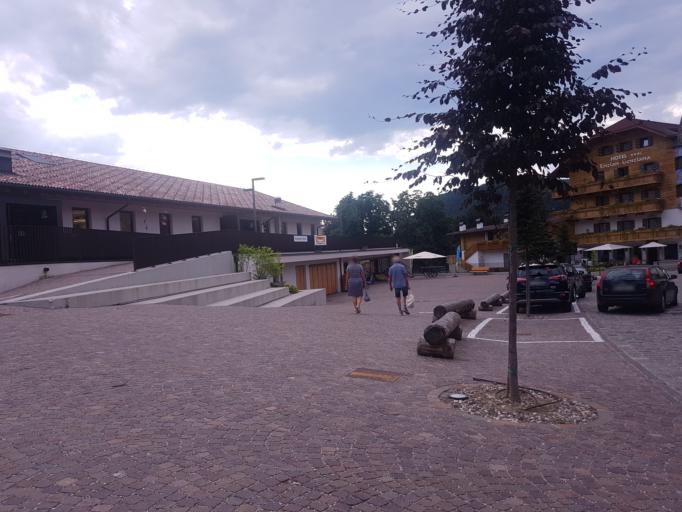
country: IT
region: Trentino-Alto Adige
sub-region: Bolzano
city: Siusi
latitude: 46.5444
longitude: 11.5603
